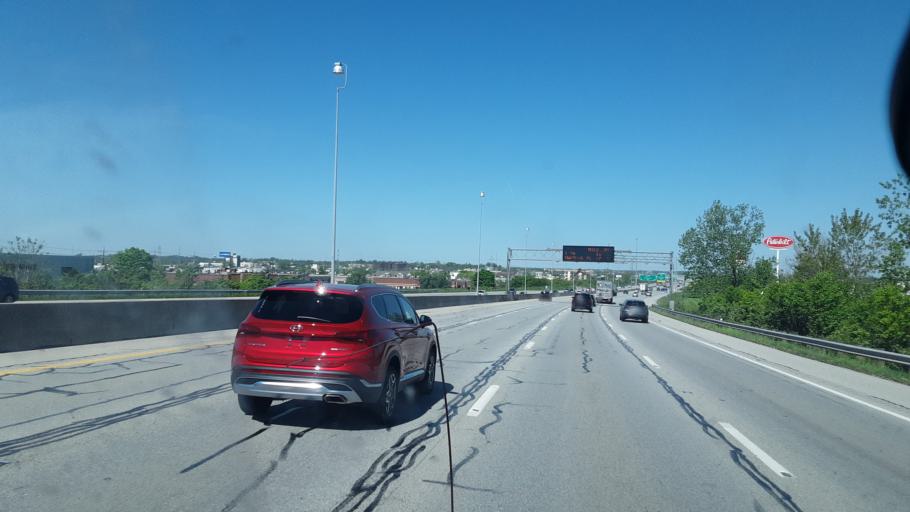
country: US
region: Ohio
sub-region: Hamilton County
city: Sharonville
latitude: 39.2852
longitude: -84.4189
